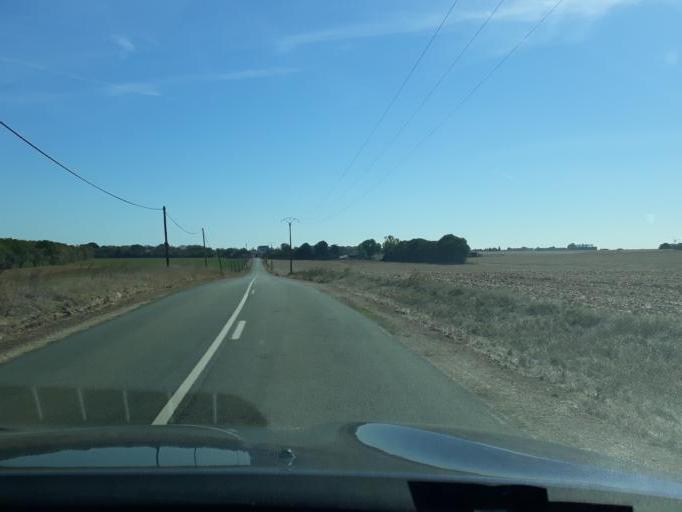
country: FR
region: Centre
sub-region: Departement du Loir-et-Cher
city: Ouzouer-le-Marche
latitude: 47.9328
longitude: 1.5163
